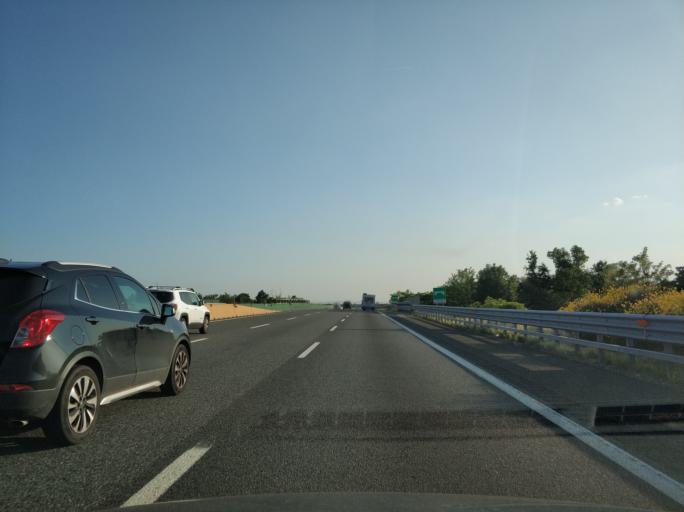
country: IT
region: Piedmont
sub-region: Provincia di Vercelli
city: Santhia
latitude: 45.4013
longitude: 8.1593
